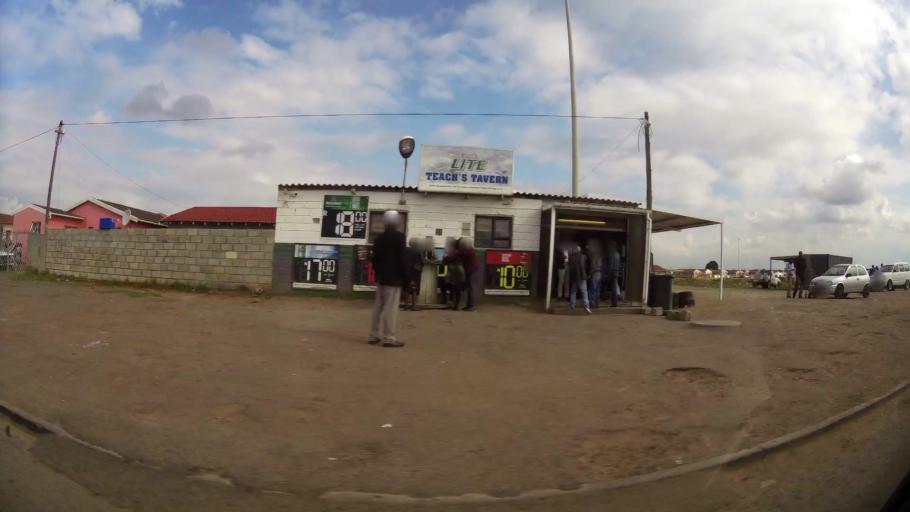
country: ZA
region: Eastern Cape
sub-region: Nelson Mandela Bay Metropolitan Municipality
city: Port Elizabeth
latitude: -33.8157
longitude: 25.5932
